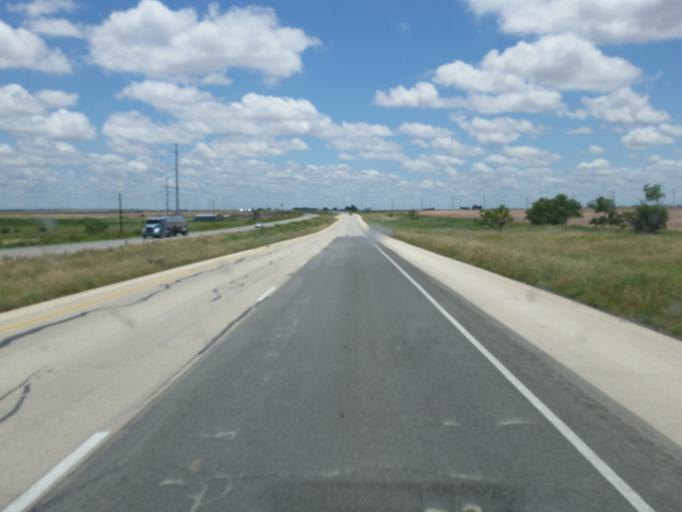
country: US
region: Texas
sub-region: Nolan County
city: Roscoe
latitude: 32.4949
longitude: -100.6363
